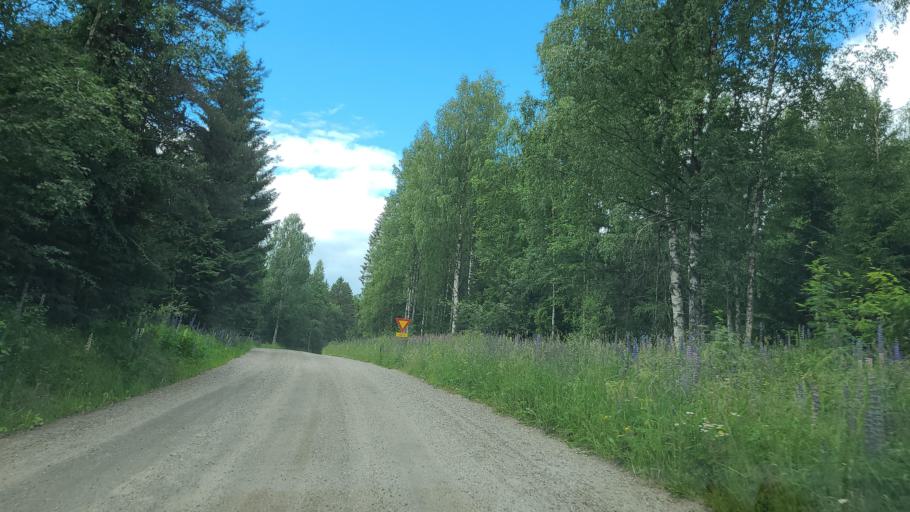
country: FI
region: Northern Savo
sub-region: Koillis-Savo
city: Kaavi
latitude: 62.9880
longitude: 28.5101
